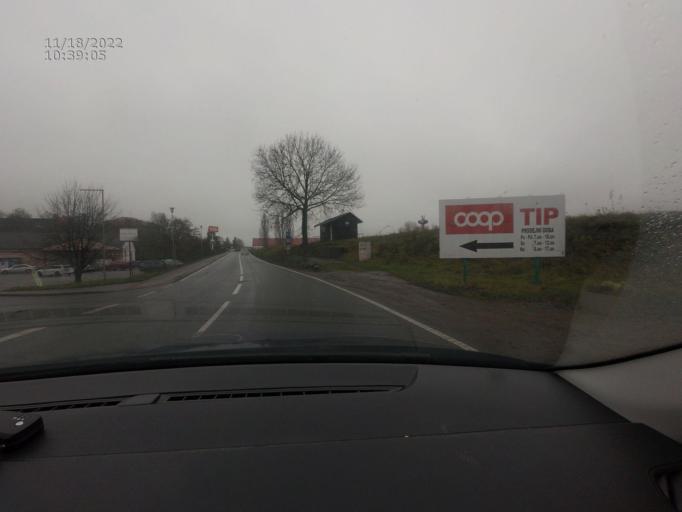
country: CZ
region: Central Bohemia
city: Zebrak
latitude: 49.8731
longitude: 13.8931
